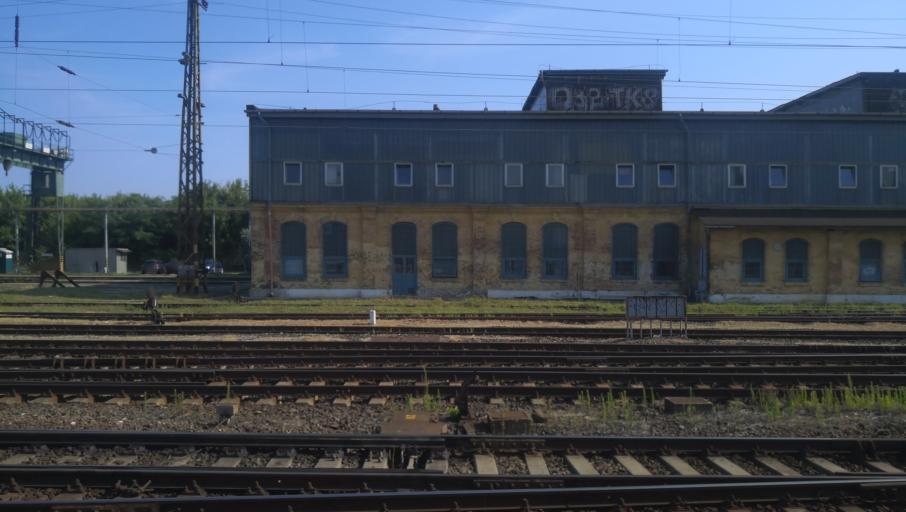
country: HU
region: Budapest
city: Budapest X. keruelet
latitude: 47.4897
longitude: 19.1679
